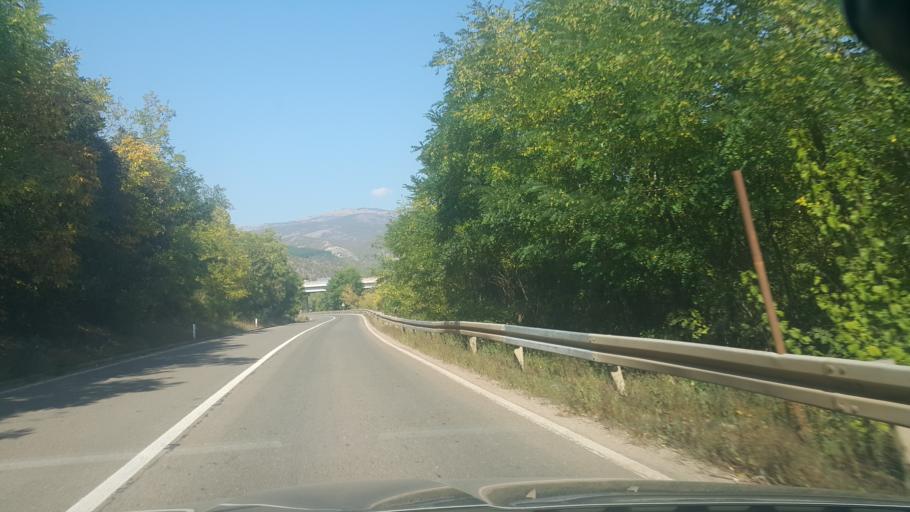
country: RS
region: Central Serbia
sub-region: Pirotski Okrug
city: Bela Palanka
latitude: 43.2564
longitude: 22.2614
